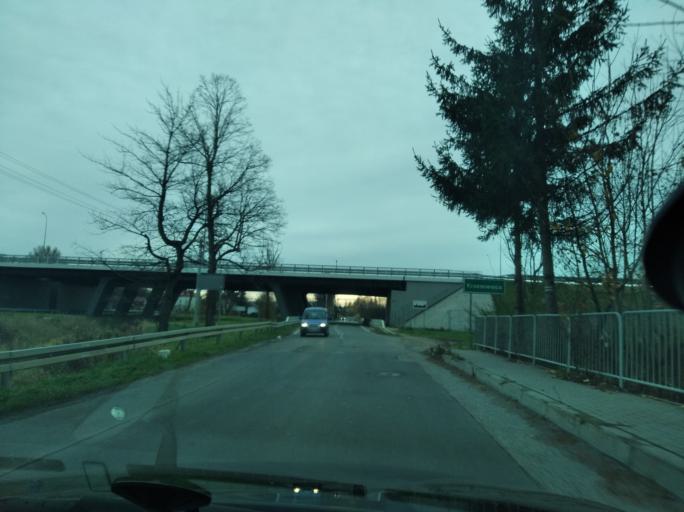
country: PL
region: Subcarpathian Voivodeship
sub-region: Powiat lancucki
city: Czarna
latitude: 50.0914
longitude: 22.1843
